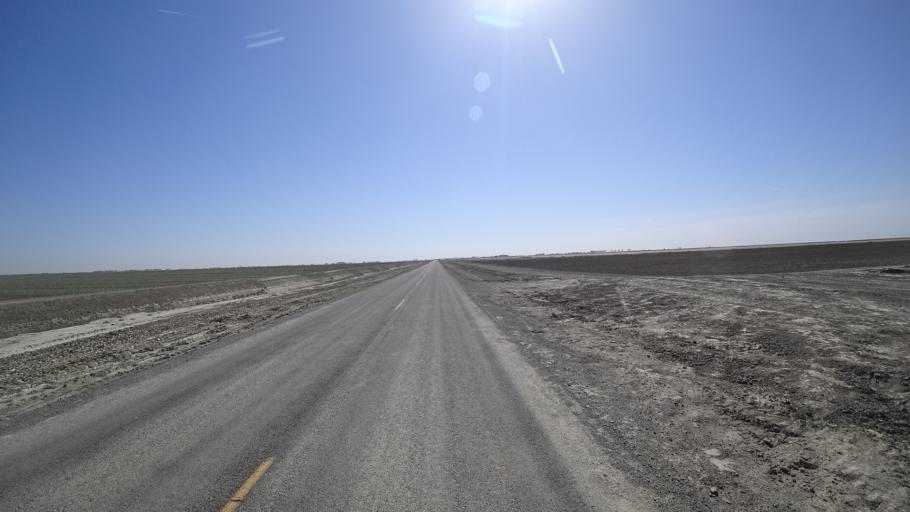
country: US
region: California
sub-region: Tulare County
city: Alpaugh
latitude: 35.8914
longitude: -119.5471
